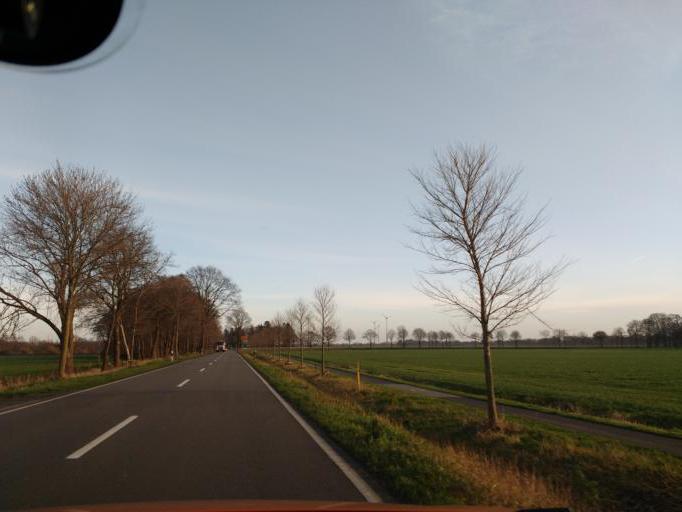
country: DE
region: Lower Saxony
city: Hatten
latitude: 53.1287
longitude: 8.3318
